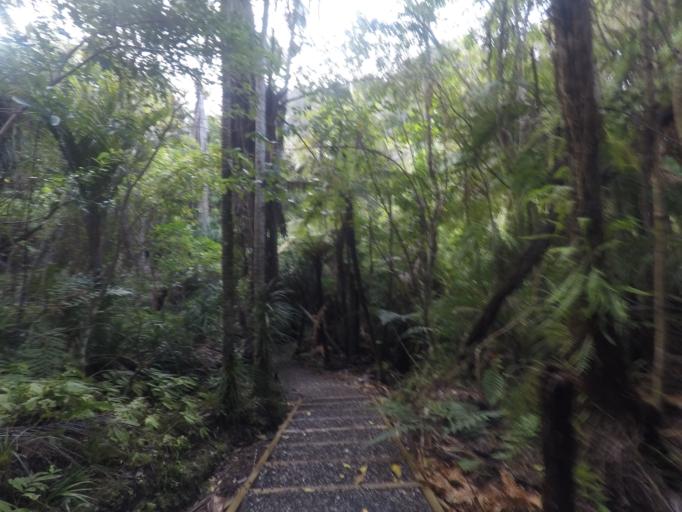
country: NZ
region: Auckland
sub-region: Auckland
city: Titirangi
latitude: -37.0012
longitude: 174.5500
